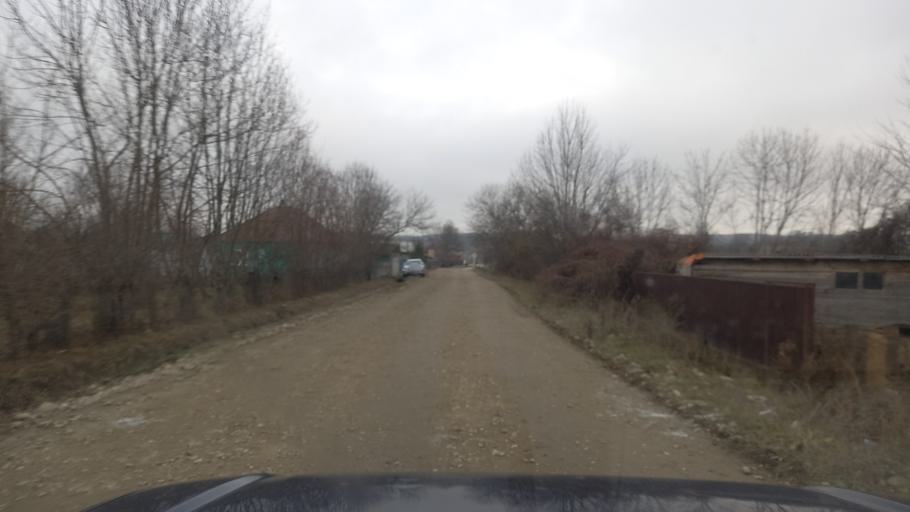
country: RU
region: Krasnodarskiy
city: Neftegorsk
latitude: 44.2483
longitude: 39.7619
